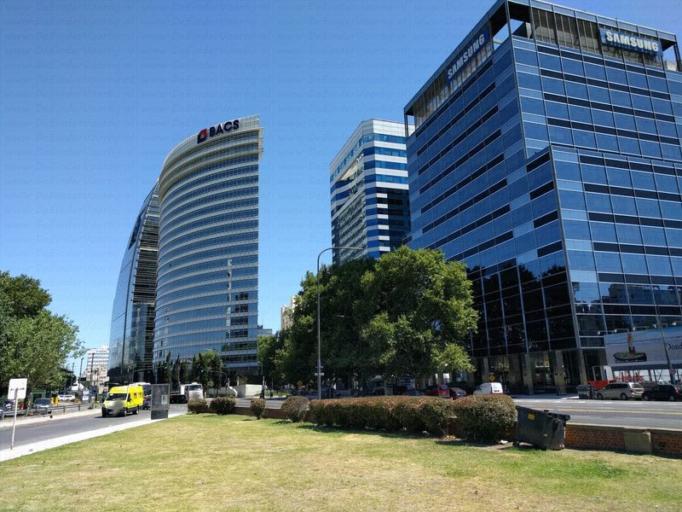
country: AR
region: Buenos Aires F.D.
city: Buenos Aires
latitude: -34.5984
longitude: -58.3692
